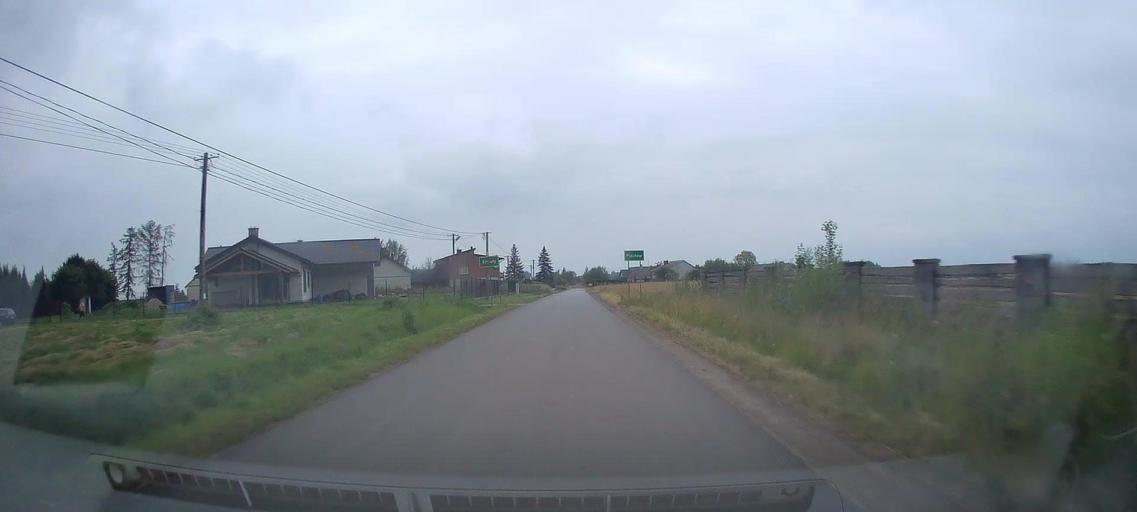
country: PL
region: Masovian Voivodeship
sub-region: Powiat radomski
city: Jedlinsk
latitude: 51.4715
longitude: 21.1107
